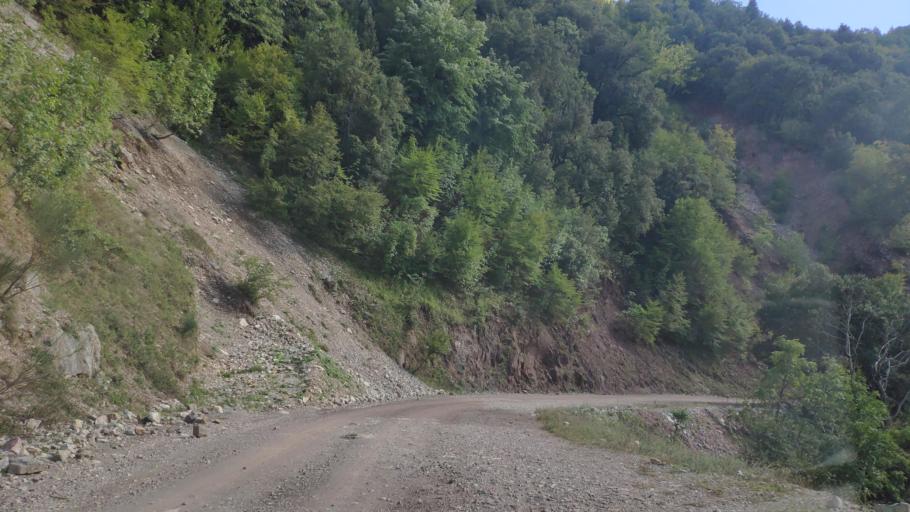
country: GR
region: Central Greece
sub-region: Nomos Evrytanias
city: Kerasochori
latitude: 39.1091
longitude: 21.6143
